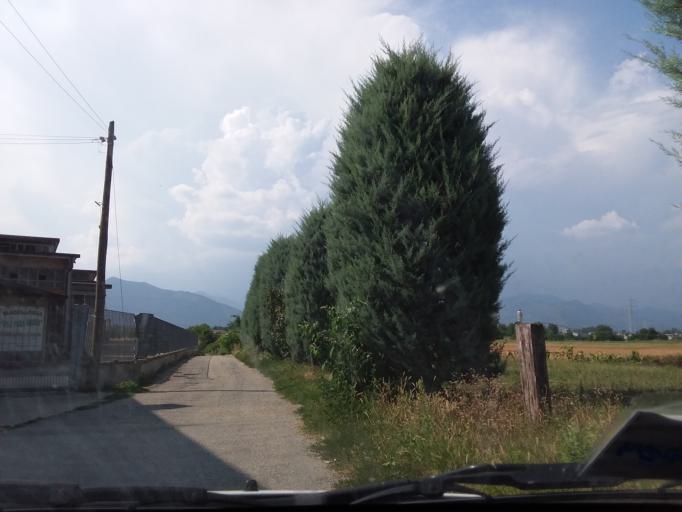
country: IT
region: Piedmont
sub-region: Provincia di Torino
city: Pianezza
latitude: 45.0863
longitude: 7.5425
